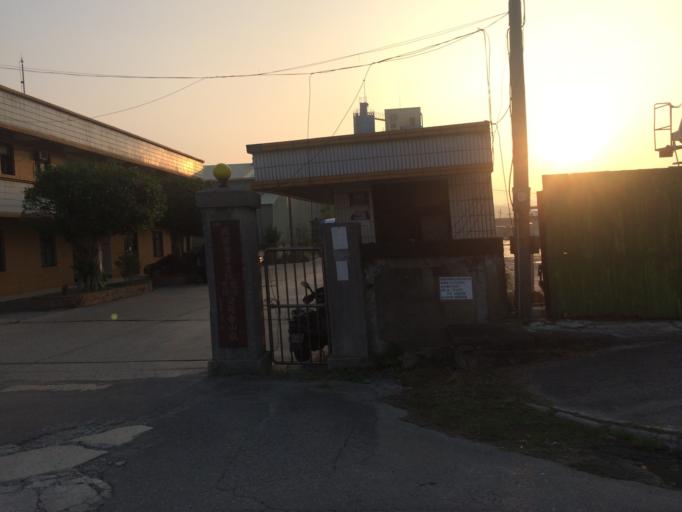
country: TW
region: Taiwan
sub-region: Hsinchu
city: Hsinchu
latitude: 24.7317
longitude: 120.9153
